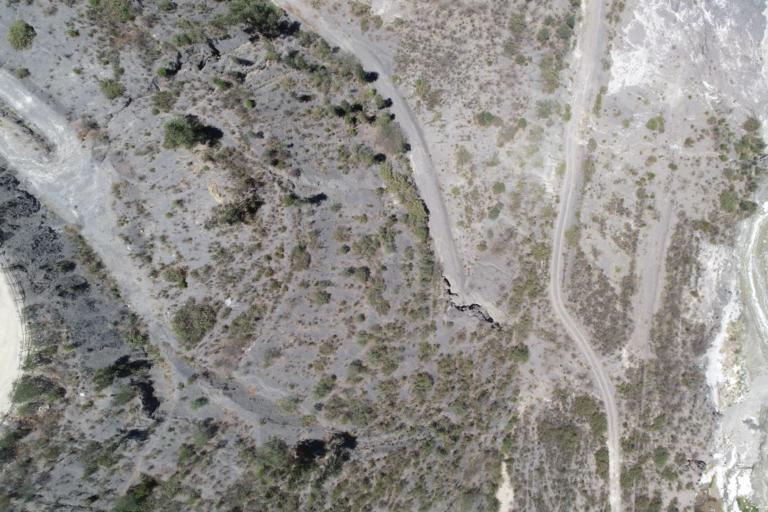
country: BO
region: La Paz
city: La Paz
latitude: -16.6141
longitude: -68.0622
